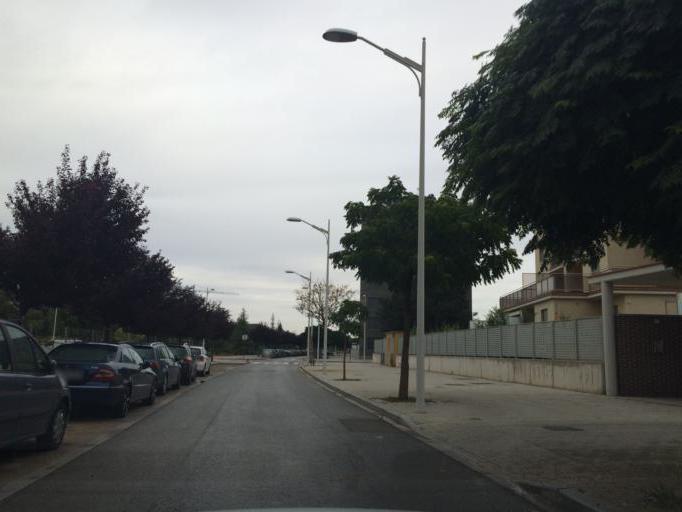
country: ES
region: Castille-La Mancha
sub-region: Provincia de Albacete
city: Albacete
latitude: 39.0067
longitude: -1.8567
